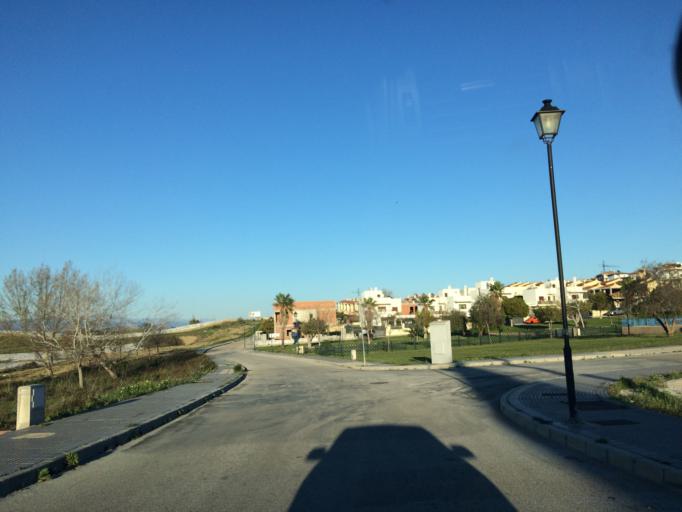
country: ES
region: Andalusia
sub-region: Provincia de Malaga
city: Alhaurin de la Torre
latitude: 36.6665
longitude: -4.5397
